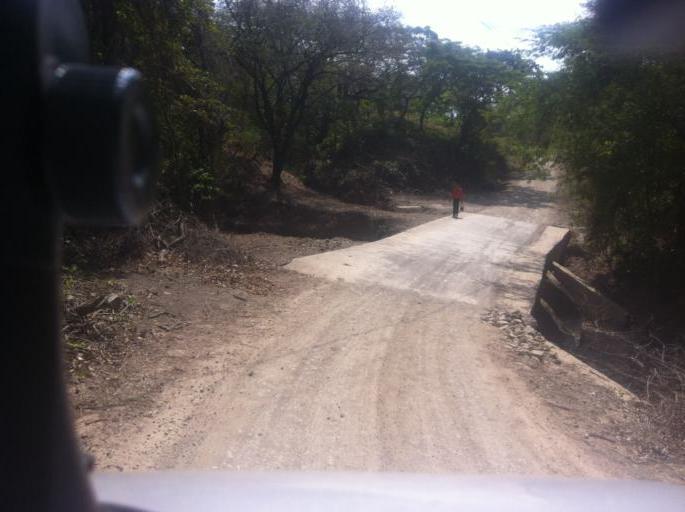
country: NI
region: Rivas
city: Belen
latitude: 11.5778
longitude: -86.0229
